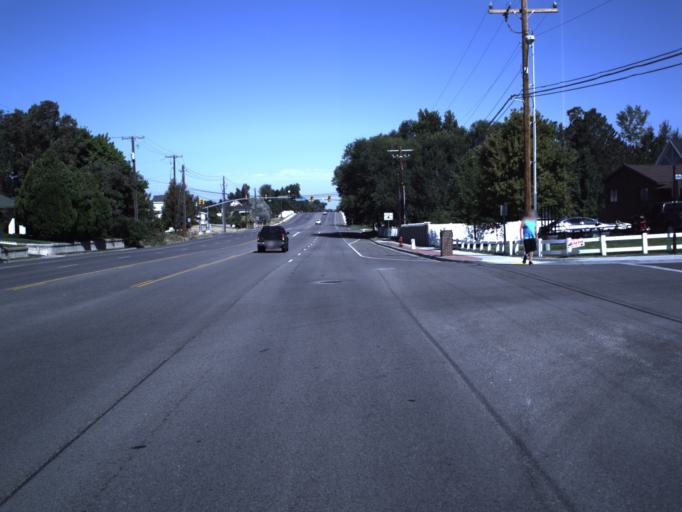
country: US
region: Utah
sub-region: Davis County
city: Fruit Heights
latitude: 41.0150
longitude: -111.9166
